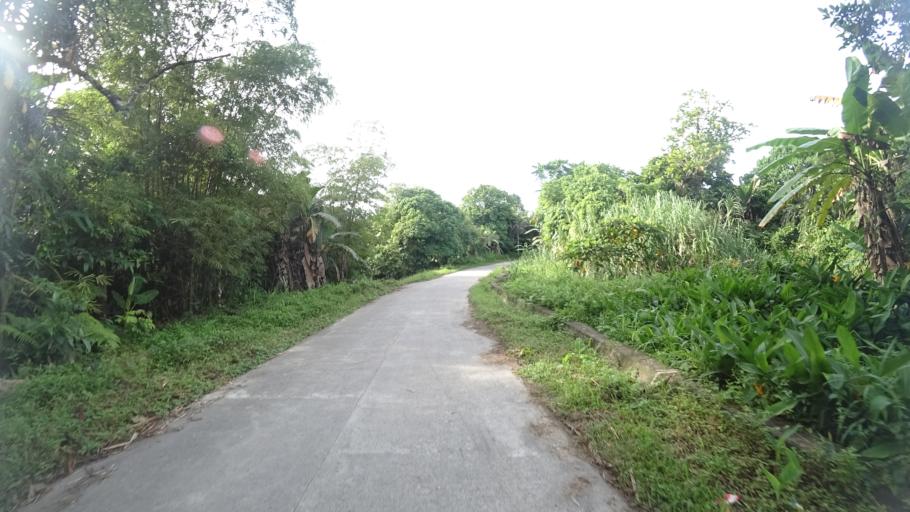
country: PH
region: Eastern Visayas
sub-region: Province of Leyte
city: Pastrana
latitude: 11.1681
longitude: 124.8696
